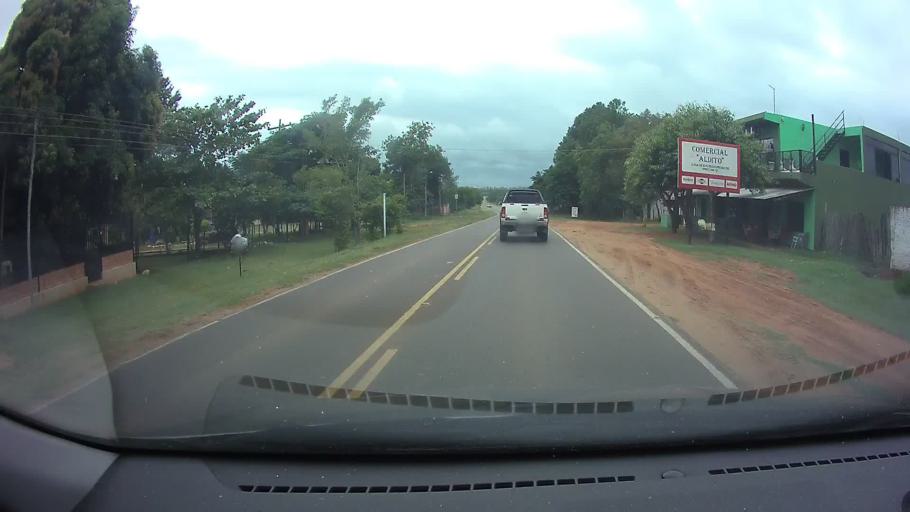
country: PY
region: Central
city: Nueva Italia
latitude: -25.5957
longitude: -57.5064
